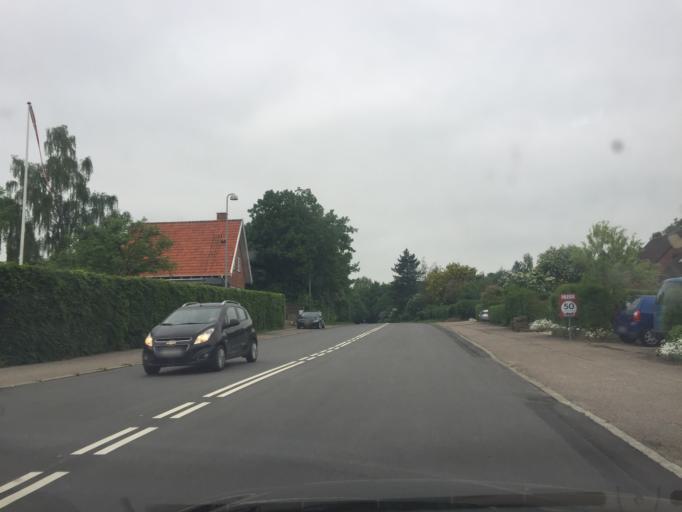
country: DK
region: Capital Region
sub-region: Hoje-Taastrup Kommune
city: Taastrup
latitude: 55.6602
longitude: 12.3091
